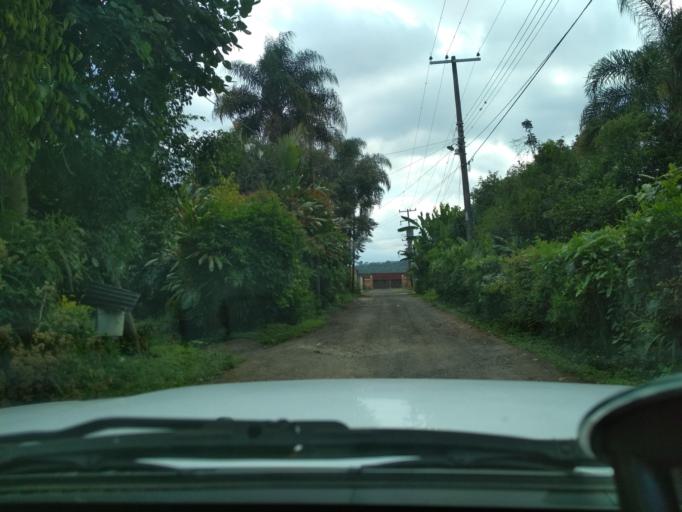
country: MX
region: Veracruz
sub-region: Fortin
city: Monte Salas
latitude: 18.9342
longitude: -97.0183
